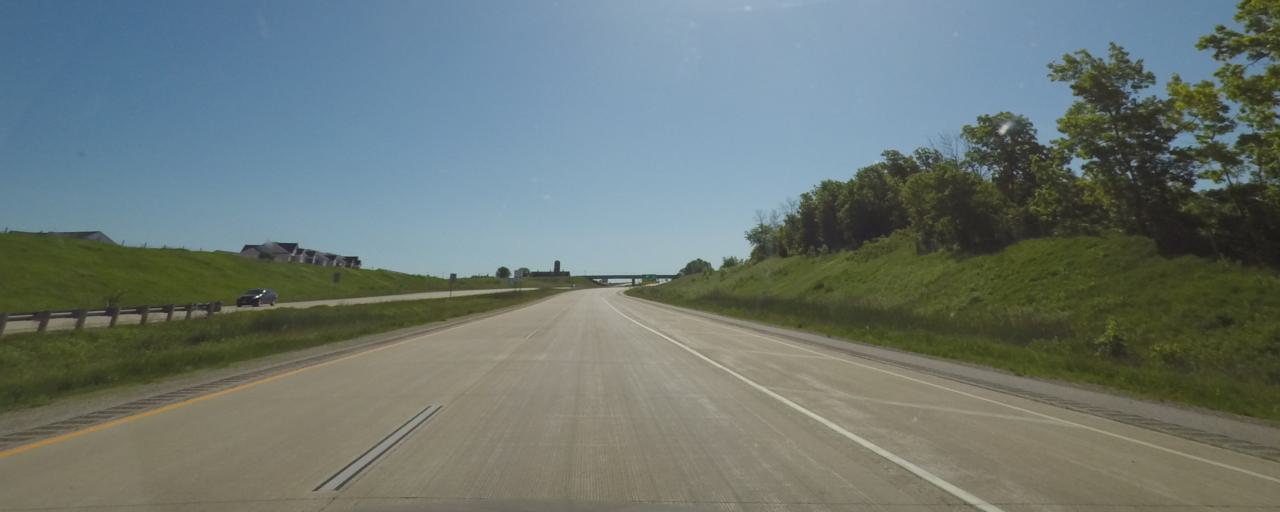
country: US
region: Wisconsin
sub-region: Fond du Lac County
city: Fond du Lac
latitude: 43.7370
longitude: -88.4568
